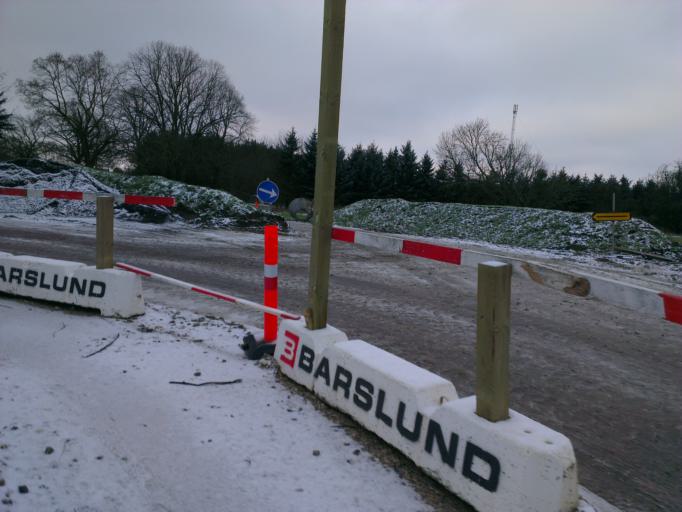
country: DK
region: Capital Region
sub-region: Frederikssund Kommune
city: Jaegerspris
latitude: 55.8575
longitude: 11.9951
